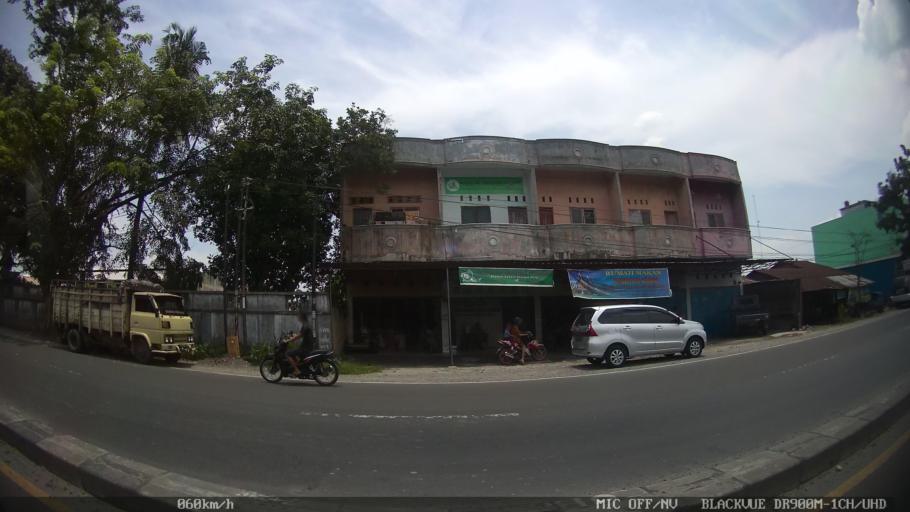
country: ID
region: North Sumatra
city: Binjai
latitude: 3.6018
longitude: 98.5422
